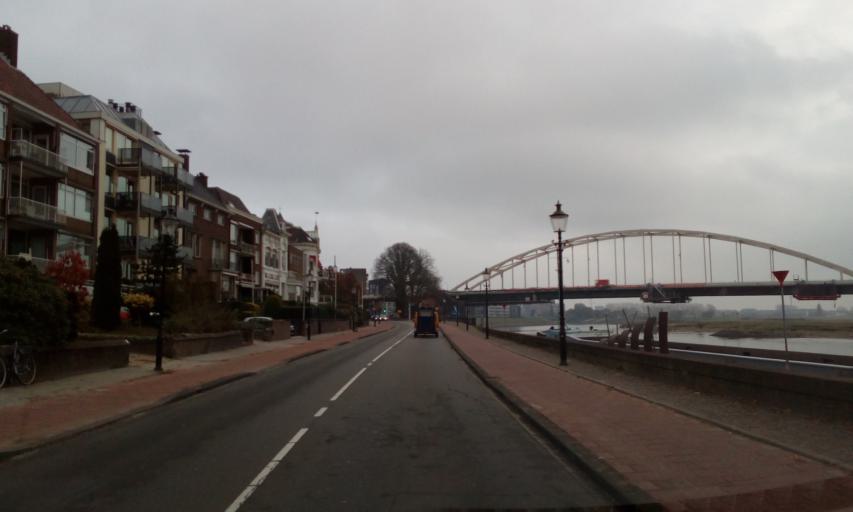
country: NL
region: Overijssel
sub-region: Gemeente Deventer
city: Deventer
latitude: 52.2505
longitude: 6.1556
